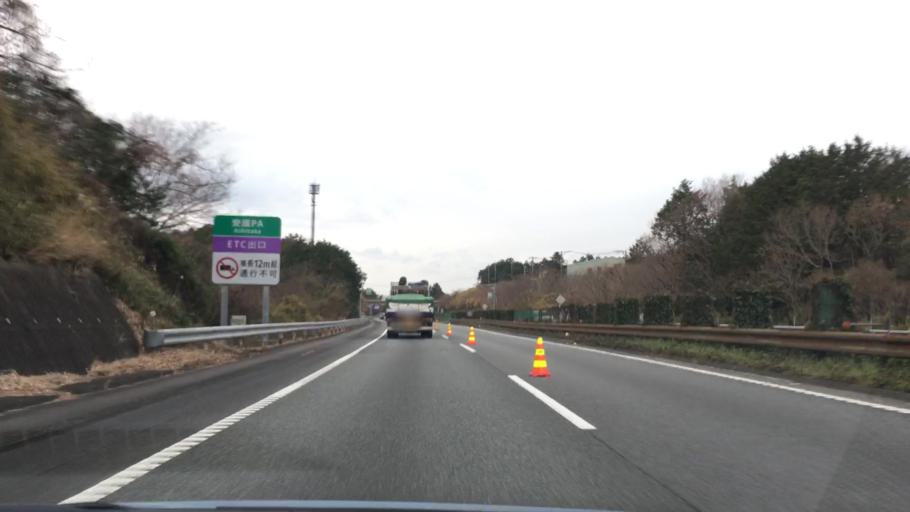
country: JP
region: Shizuoka
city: Numazu
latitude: 35.1444
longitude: 138.8480
